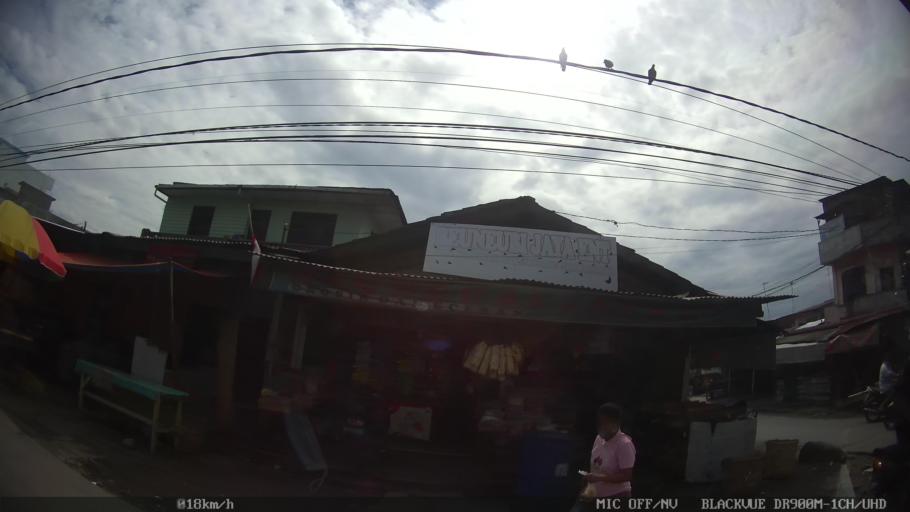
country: ID
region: North Sumatra
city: Sunggal
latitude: 3.6006
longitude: 98.6086
